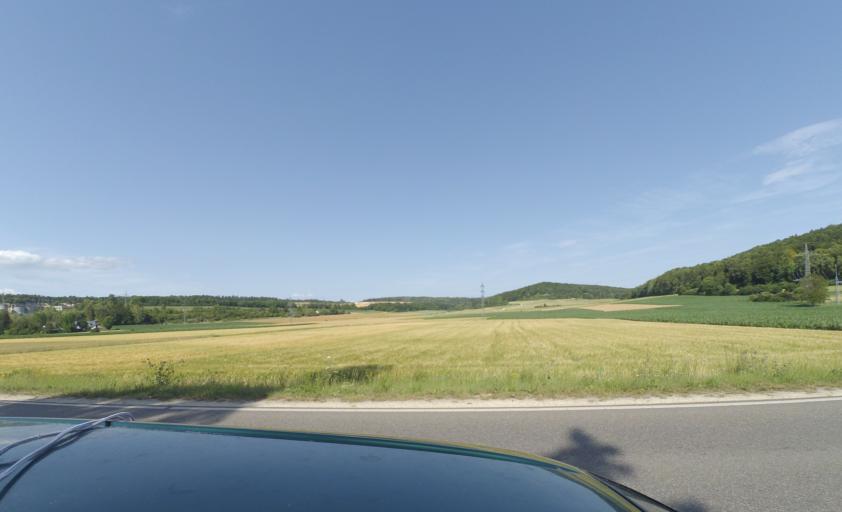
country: DE
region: Baden-Wuerttemberg
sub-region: Regierungsbezirk Stuttgart
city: Bolheim
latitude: 48.6511
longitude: 10.1650
